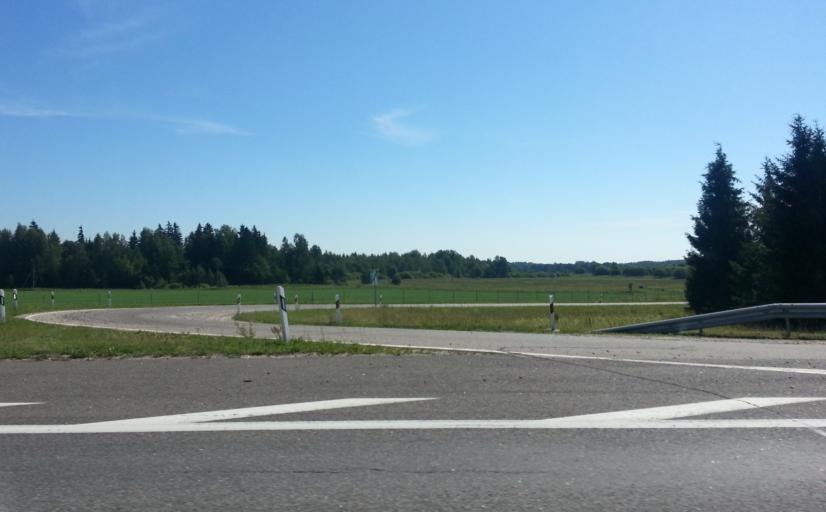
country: LT
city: Sirvintos
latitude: 55.0665
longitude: 24.8852
